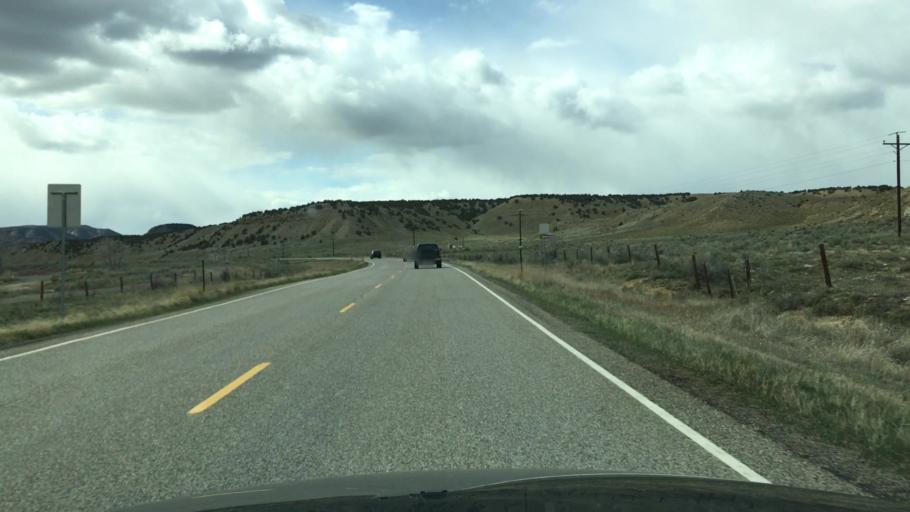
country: US
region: Colorado
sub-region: Rio Blanco County
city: Meeker
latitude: 40.0912
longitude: -108.2068
